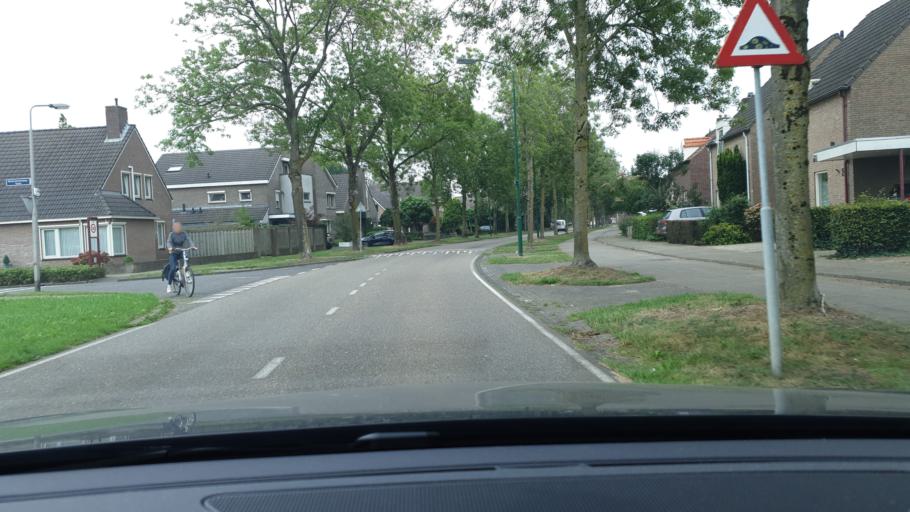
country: NL
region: North Brabant
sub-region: Gemeente Oss
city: Oss
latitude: 51.7722
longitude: 5.4975
